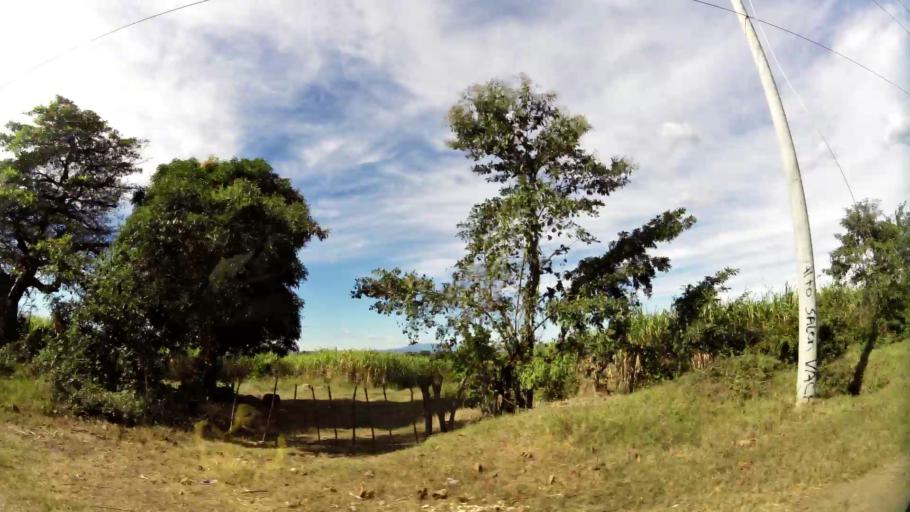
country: SV
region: San Salvador
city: Aguilares
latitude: 13.9589
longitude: -89.1371
